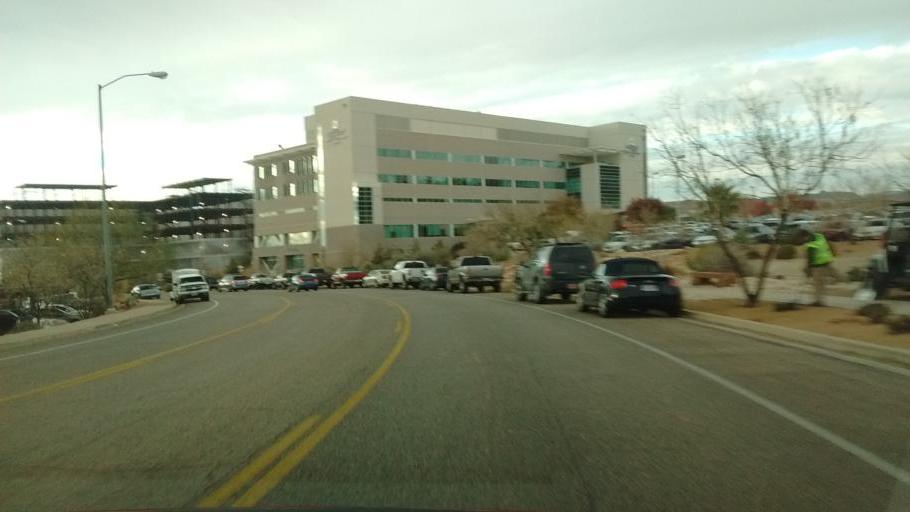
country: US
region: Utah
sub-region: Washington County
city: Saint George
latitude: 37.0960
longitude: -113.5505
